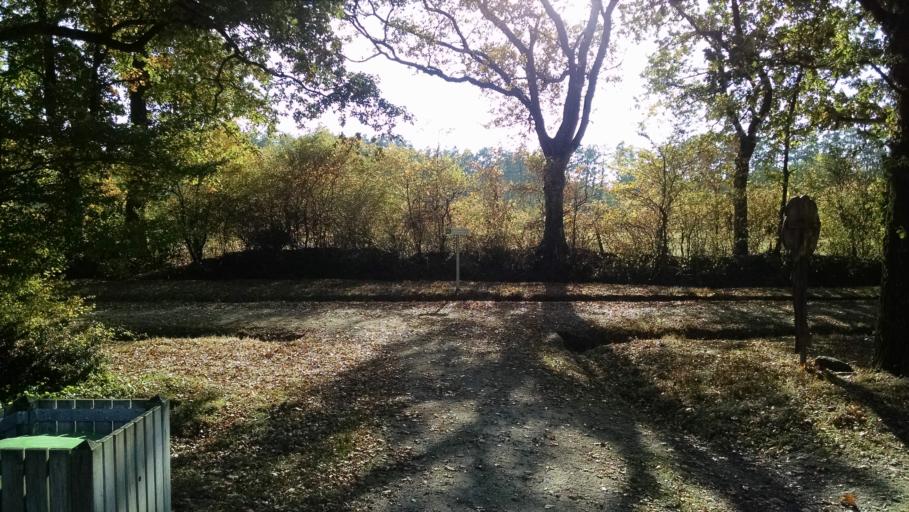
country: FR
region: Pays de la Loire
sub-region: Departement de la Vendee
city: Saint-Hilaire-de-Loulay
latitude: 47.0062
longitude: -1.3390
